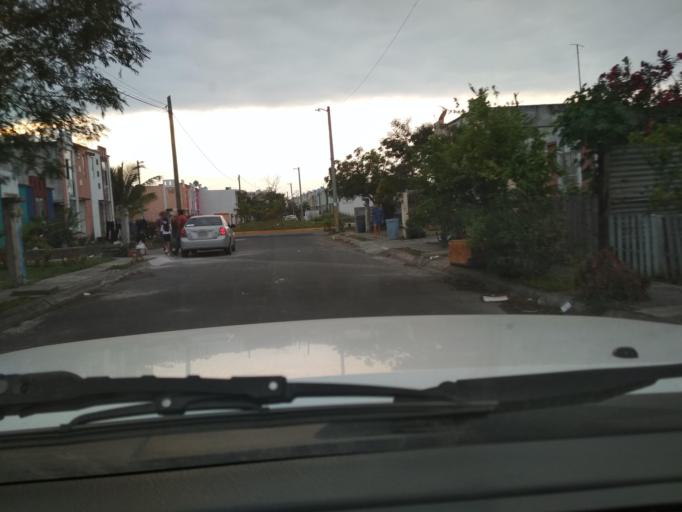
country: MX
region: Veracruz
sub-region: Medellin
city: Fraccionamiento Arboledas San Ramon
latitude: 19.0922
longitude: -96.1604
